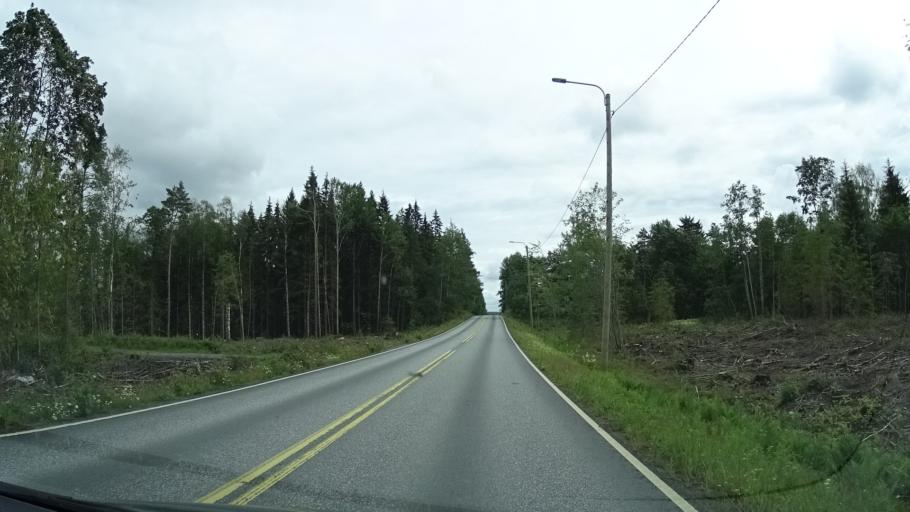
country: FI
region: Pirkanmaa
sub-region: Etelae-Pirkanmaa
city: Urjala
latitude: 61.0845
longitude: 23.4218
